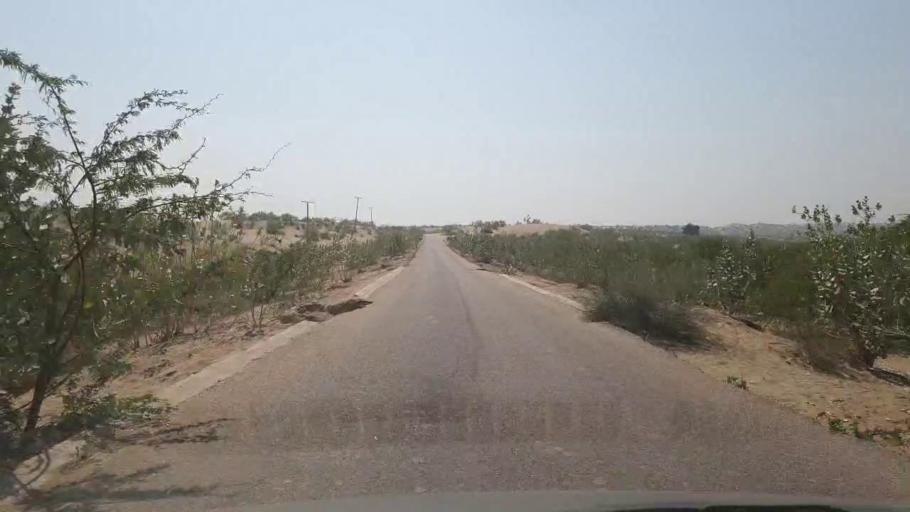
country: PK
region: Sindh
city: Chor
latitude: 25.6653
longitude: 70.1670
